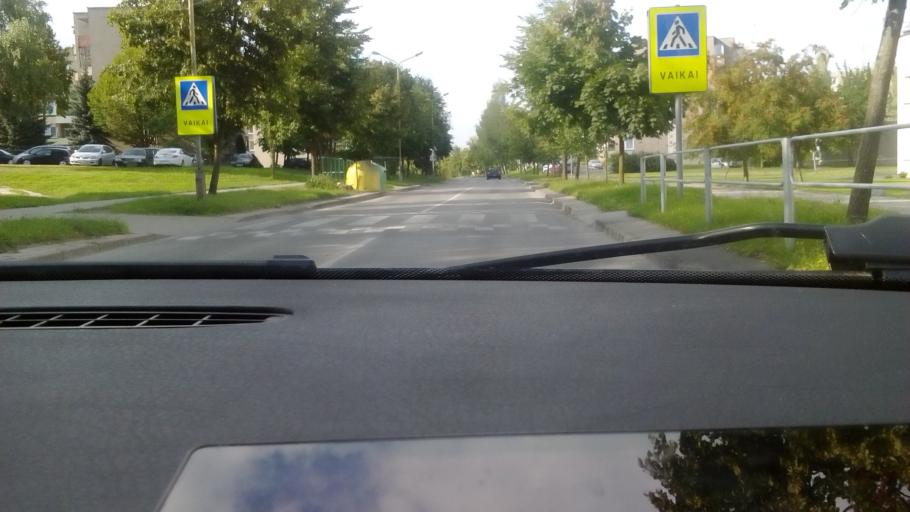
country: LT
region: Alytaus apskritis
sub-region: Alytus
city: Alytus
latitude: 54.3951
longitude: 24.0206
